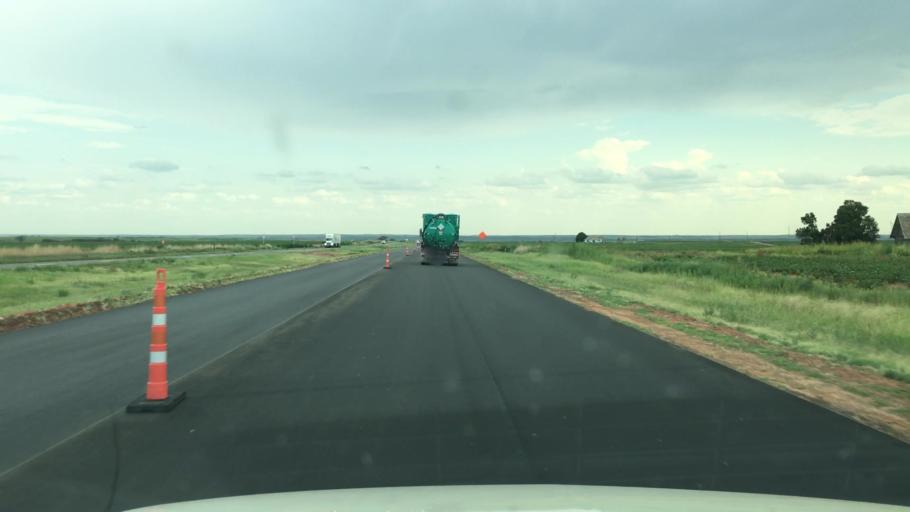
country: US
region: Texas
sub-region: Hall County
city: Memphis
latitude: 34.6205
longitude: -100.4723
